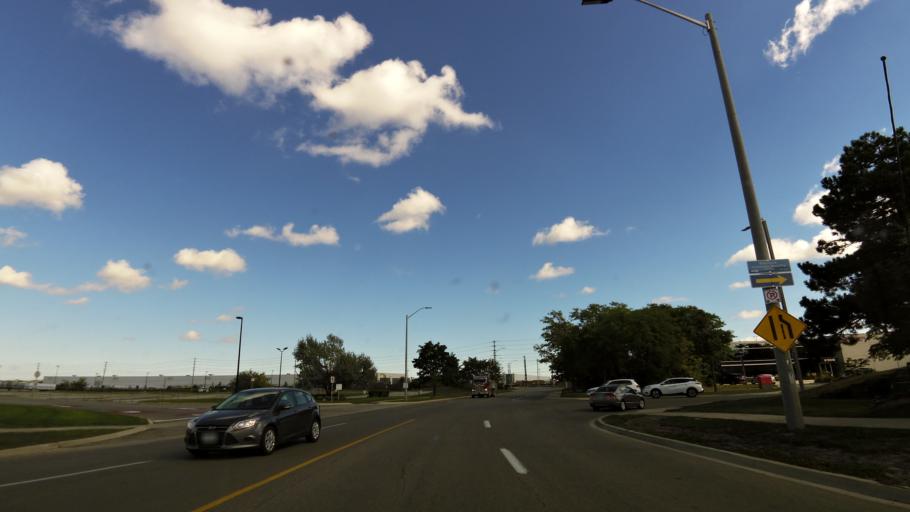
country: CA
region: Ontario
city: Mississauga
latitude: 43.5896
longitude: -79.7393
